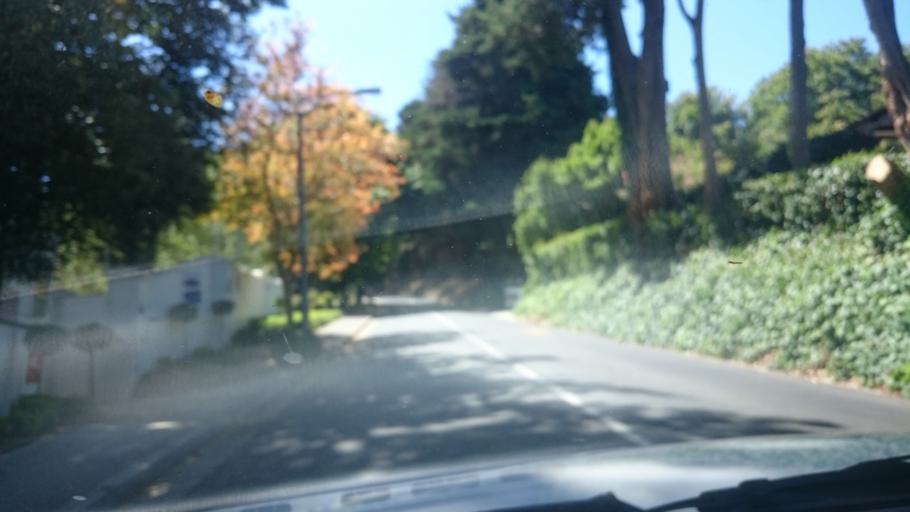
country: ZA
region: Western Cape
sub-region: City of Cape Town
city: Newlands
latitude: -33.9974
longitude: 18.4473
